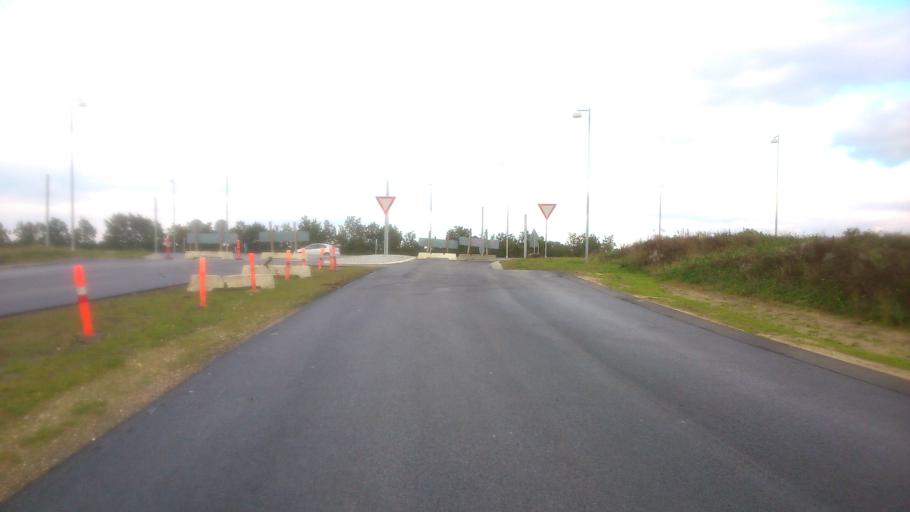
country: DK
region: Central Jutland
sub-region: Silkeborg Kommune
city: Silkeborg
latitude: 56.2025
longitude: 9.5120
